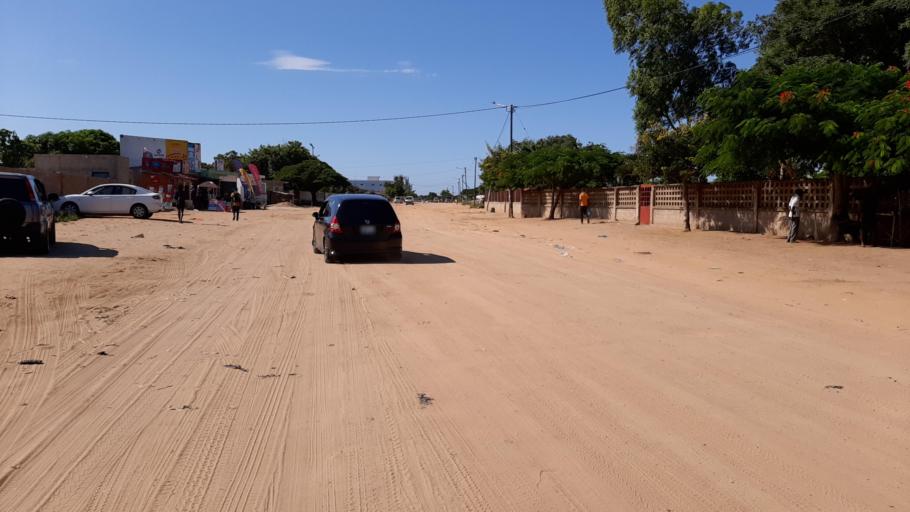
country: MZ
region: Maputo City
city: Maputo
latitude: -25.8089
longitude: 32.5462
